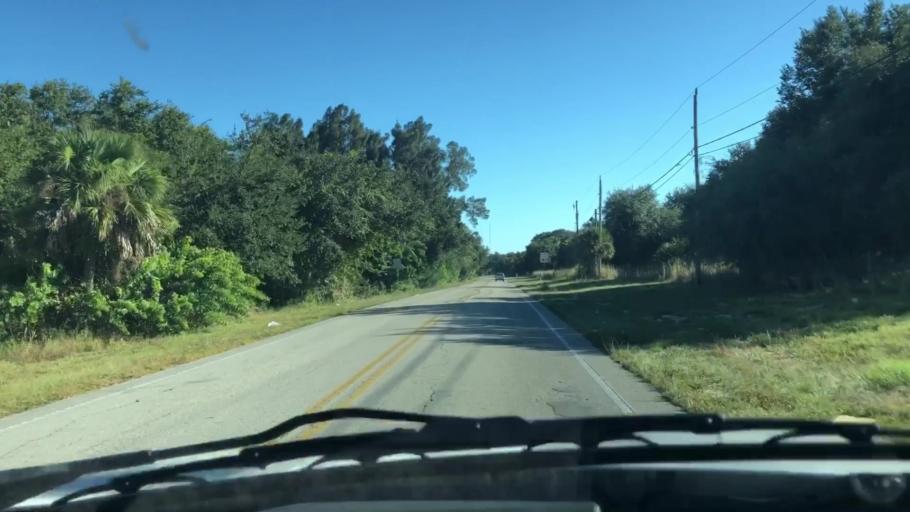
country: US
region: Florida
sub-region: Indian River County
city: Florida Ridge
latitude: 27.5704
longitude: -80.3743
